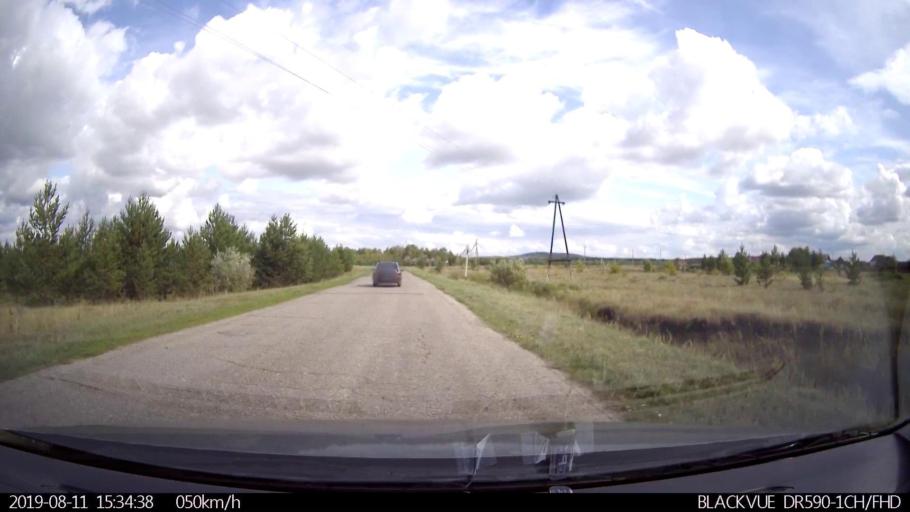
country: RU
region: Ulyanovsk
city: Ignatovka
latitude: 53.8608
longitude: 47.5977
